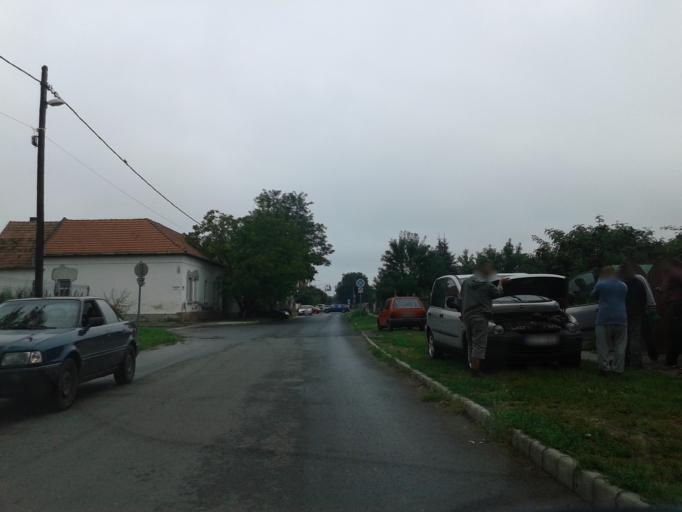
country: HU
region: Csongrad
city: Szeged
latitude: 46.2455
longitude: 20.1248
